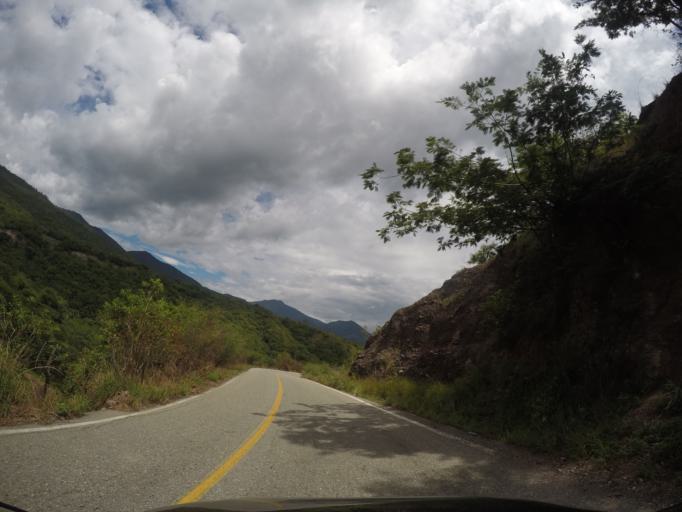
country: MX
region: Oaxaca
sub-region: San Jeronimo Coatlan
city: San Cristobal Honduras
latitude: 16.4344
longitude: -97.0577
